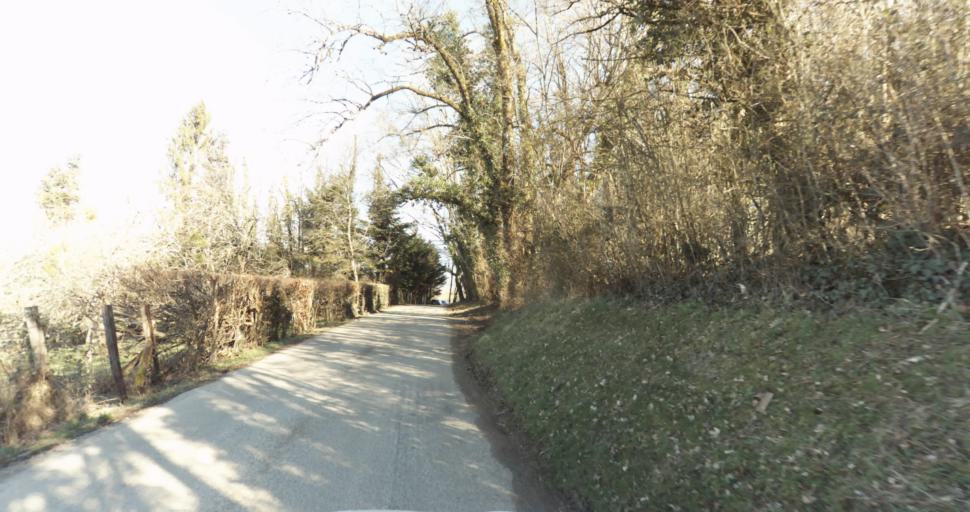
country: FR
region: Franche-Comte
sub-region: Departement du Jura
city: Lons-le-Saunier
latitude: 46.6912
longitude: 5.5437
